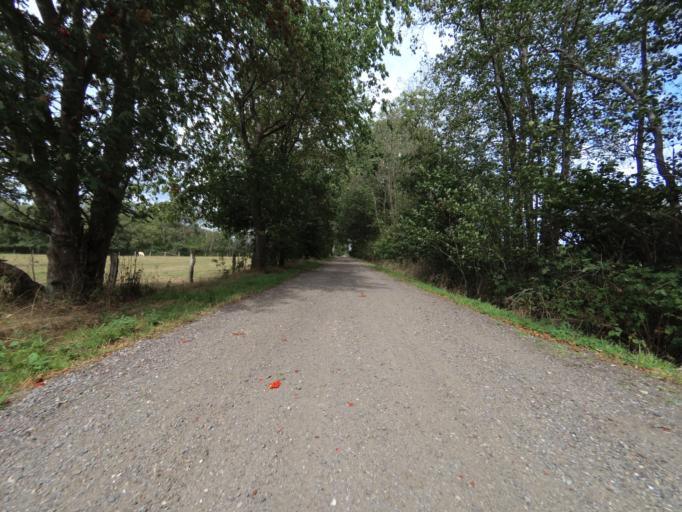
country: DE
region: North Rhine-Westphalia
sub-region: Regierungsbezirk Munster
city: Gronau
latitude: 52.1839
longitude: 6.9660
